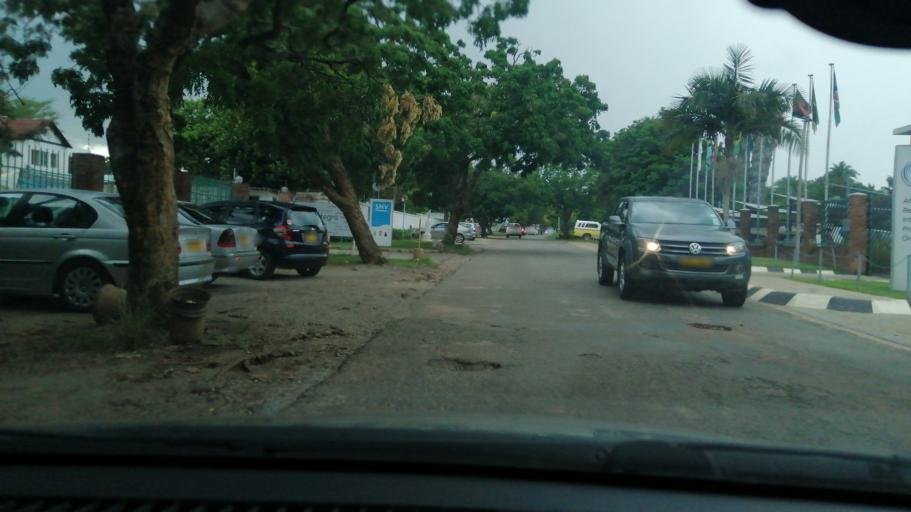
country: ZW
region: Harare
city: Harare
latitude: -17.7993
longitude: 31.0435
